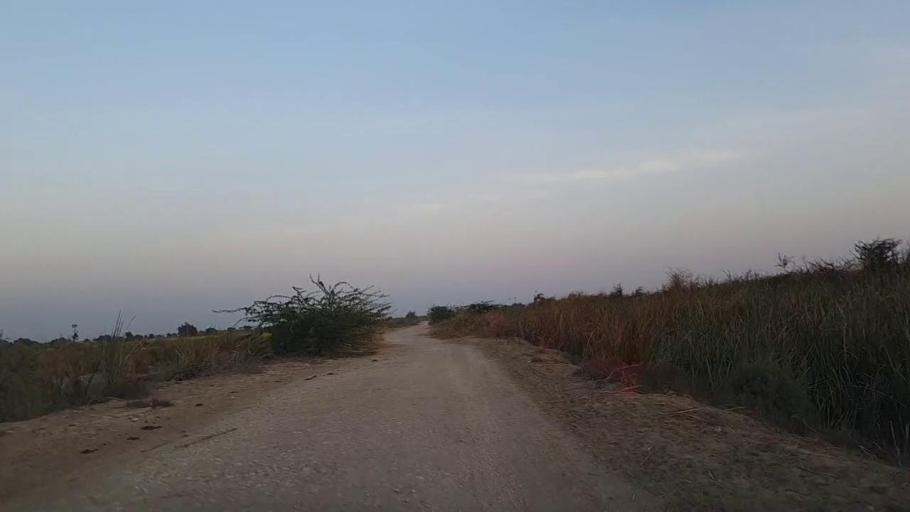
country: PK
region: Sindh
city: Tando Mittha Khan
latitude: 25.9452
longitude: 69.1252
